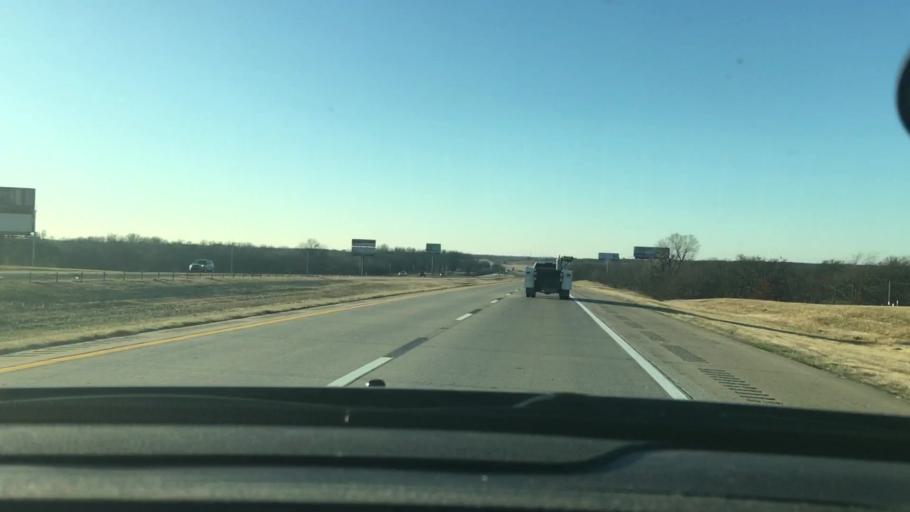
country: US
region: Oklahoma
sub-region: Carter County
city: Ardmore
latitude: 34.2741
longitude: -97.1622
